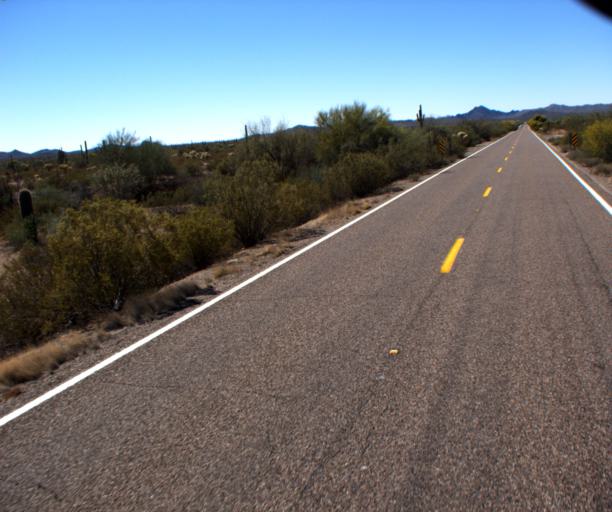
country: MX
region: Sonora
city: Sonoyta
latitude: 32.0516
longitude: -112.7908
